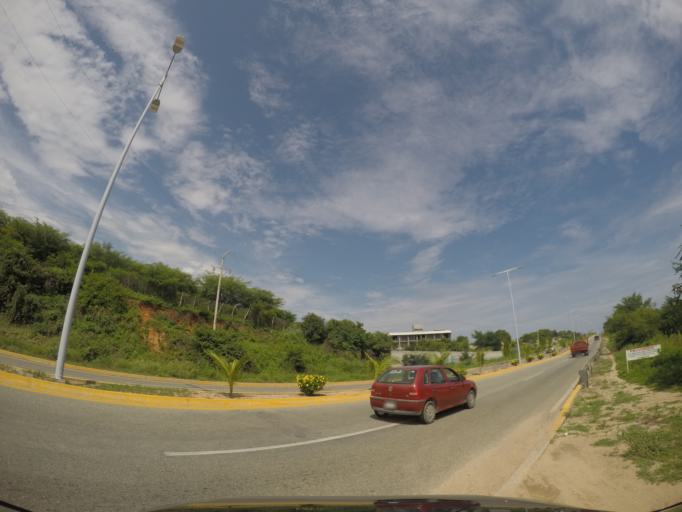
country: MX
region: Oaxaca
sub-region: Santa Maria Colotepec
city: Brisas de Zicatela
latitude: 15.8365
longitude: -97.0386
